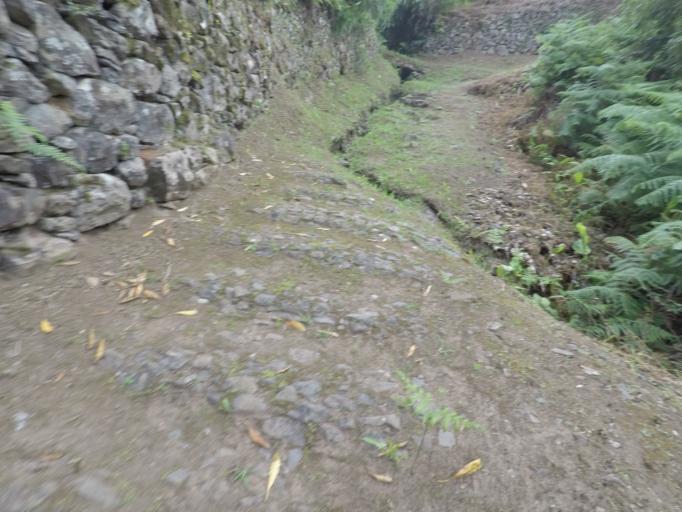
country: PT
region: Madeira
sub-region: Sao Vicente
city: Sao Vicente
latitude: 32.8178
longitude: -16.9687
